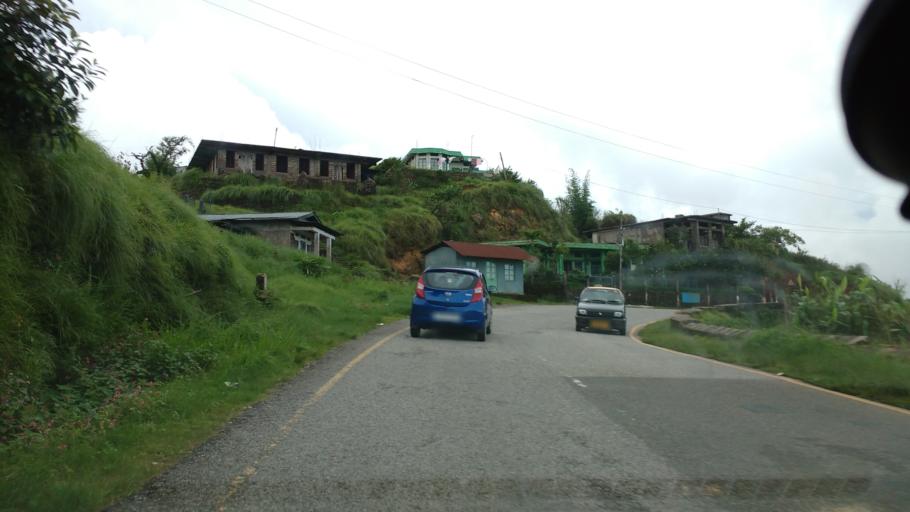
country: IN
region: Meghalaya
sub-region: East Khasi Hills
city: Cherrapunji
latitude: 25.2800
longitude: 91.7287
